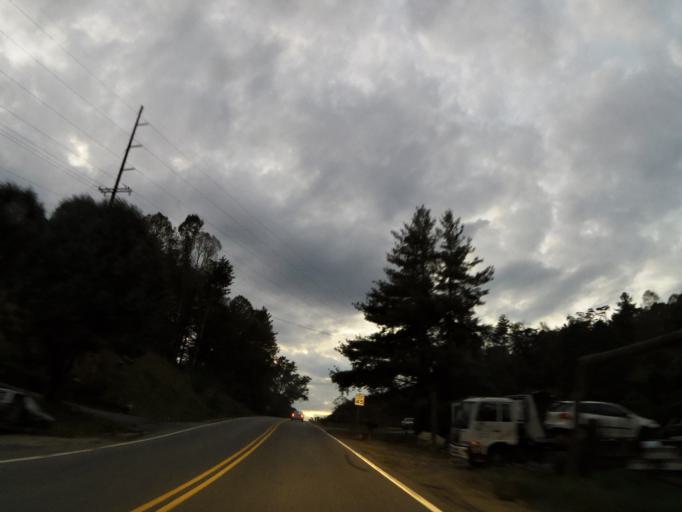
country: US
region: North Carolina
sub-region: Madison County
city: Marshall
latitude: 35.8412
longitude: -82.7218
